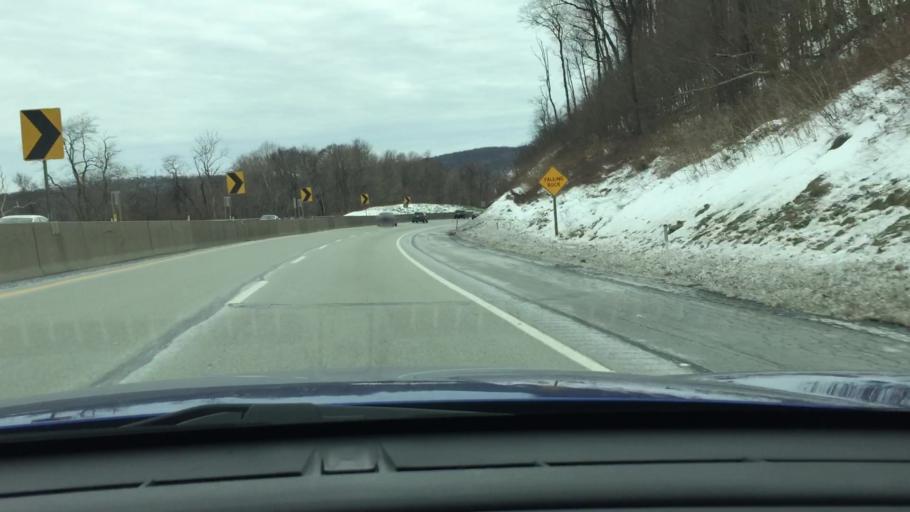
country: US
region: Pennsylvania
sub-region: Somerset County
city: Berlin
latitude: 39.9635
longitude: -78.8317
